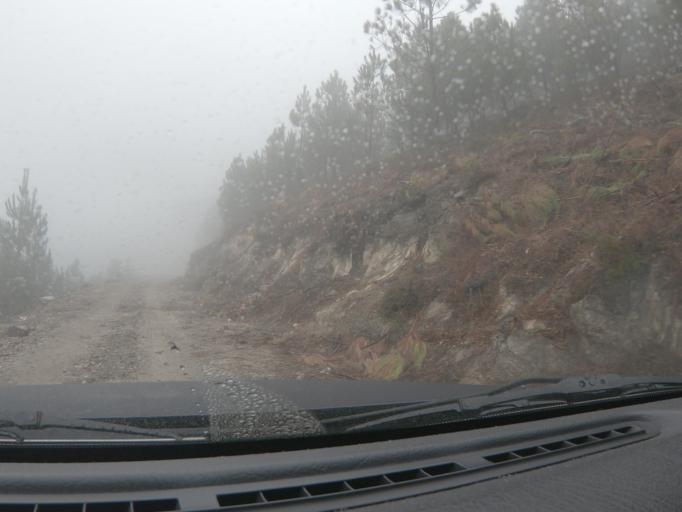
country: PT
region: Vila Real
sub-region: Vila Real
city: Vila Real
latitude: 41.3738
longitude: -7.7450
